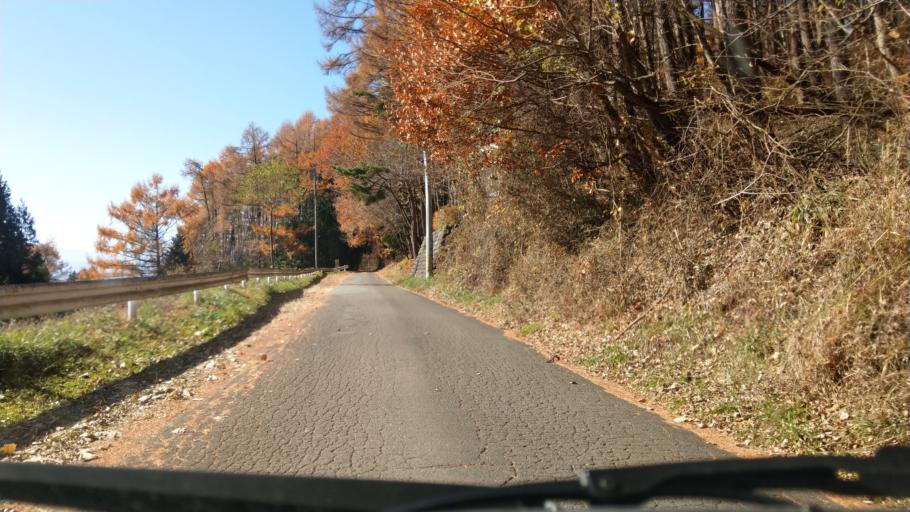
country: JP
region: Nagano
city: Komoro
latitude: 36.3620
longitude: 138.4531
